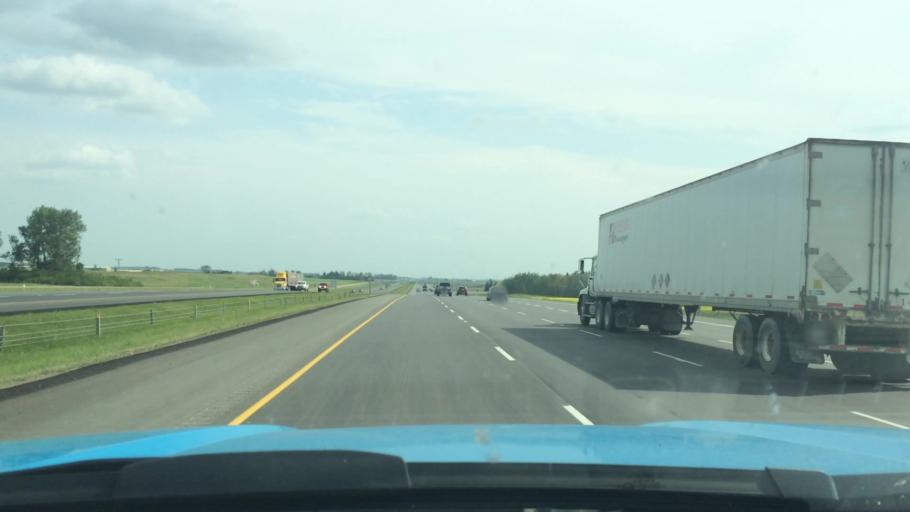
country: CA
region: Alberta
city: Crossfield
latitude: 51.3810
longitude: -114.0020
